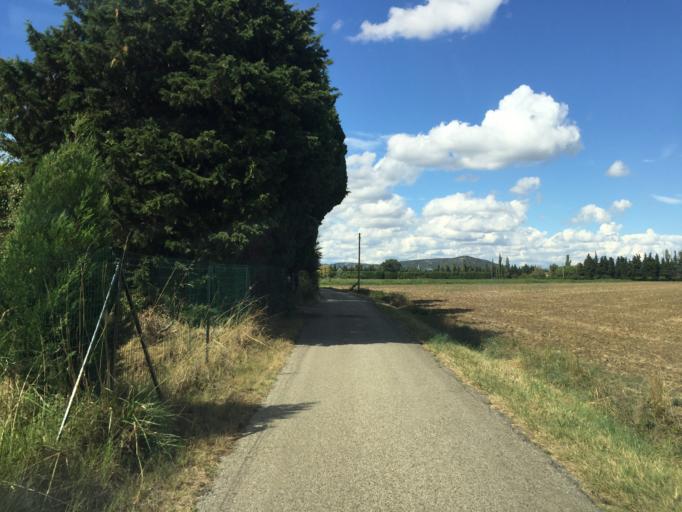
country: FR
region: Provence-Alpes-Cote d'Azur
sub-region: Departement du Vaucluse
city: Caderousse
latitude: 44.1136
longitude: 4.7322
